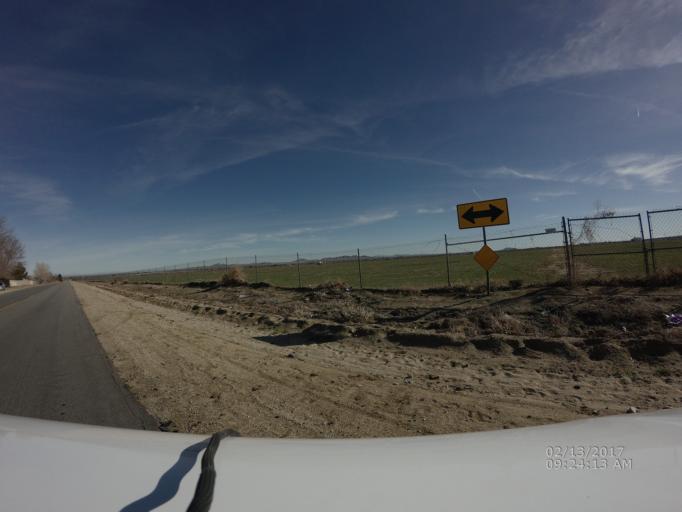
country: US
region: California
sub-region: Los Angeles County
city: Littlerock
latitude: 34.5303
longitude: -117.9581
